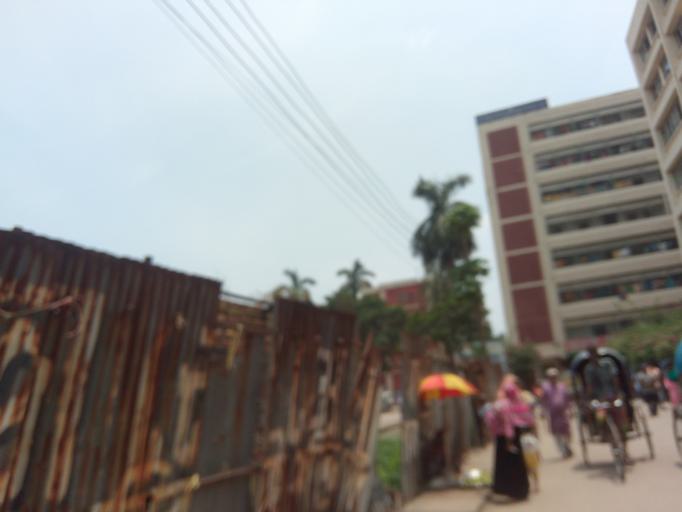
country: BD
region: Dhaka
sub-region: Dhaka
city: Dhaka
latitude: 23.7114
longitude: 90.4019
